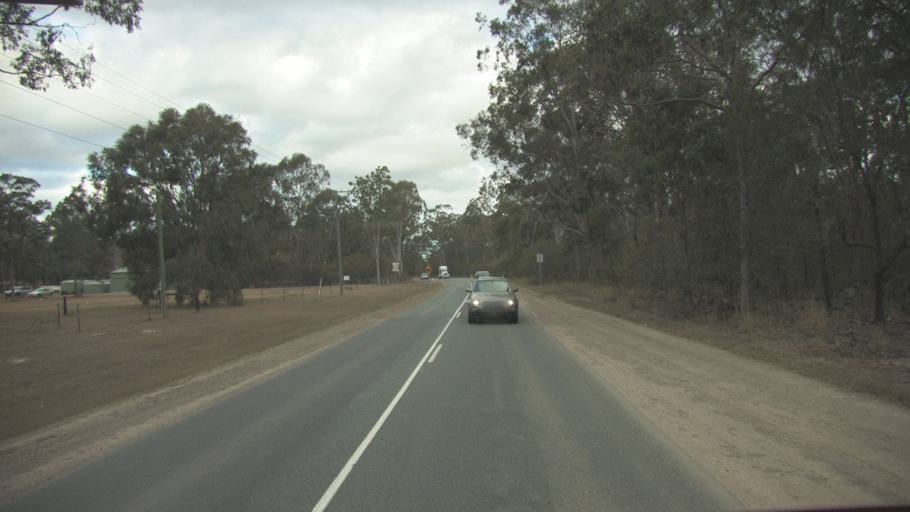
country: AU
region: Queensland
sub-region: Logan
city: Cedar Vale
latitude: -27.8603
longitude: 153.0556
